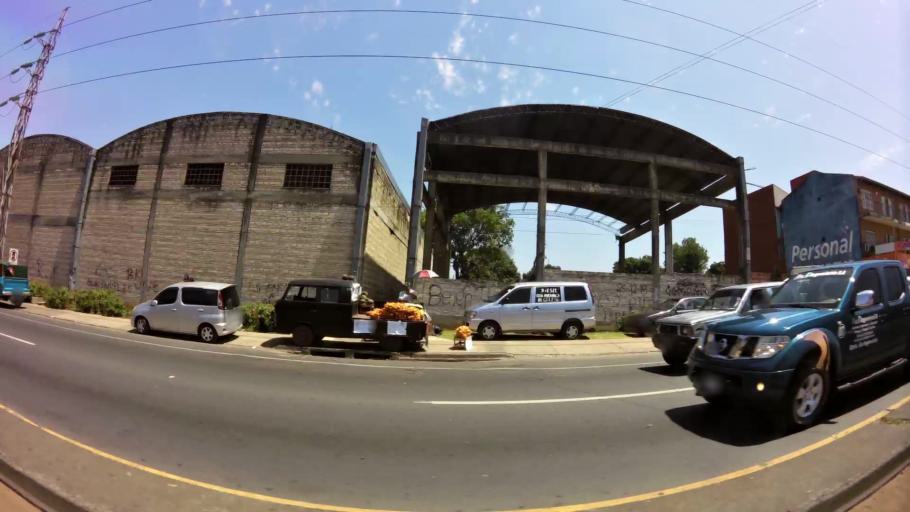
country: PY
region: Central
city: Villa Elisa
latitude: -25.3547
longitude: -57.5708
